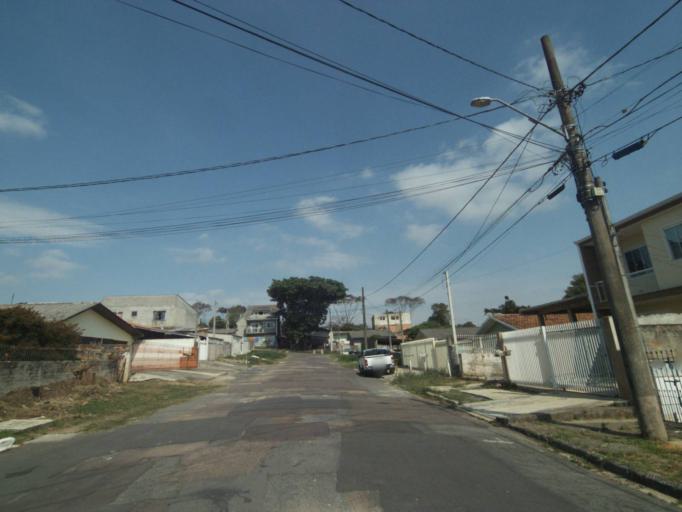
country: BR
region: Parana
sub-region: Curitiba
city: Curitiba
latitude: -25.4853
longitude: -49.3304
